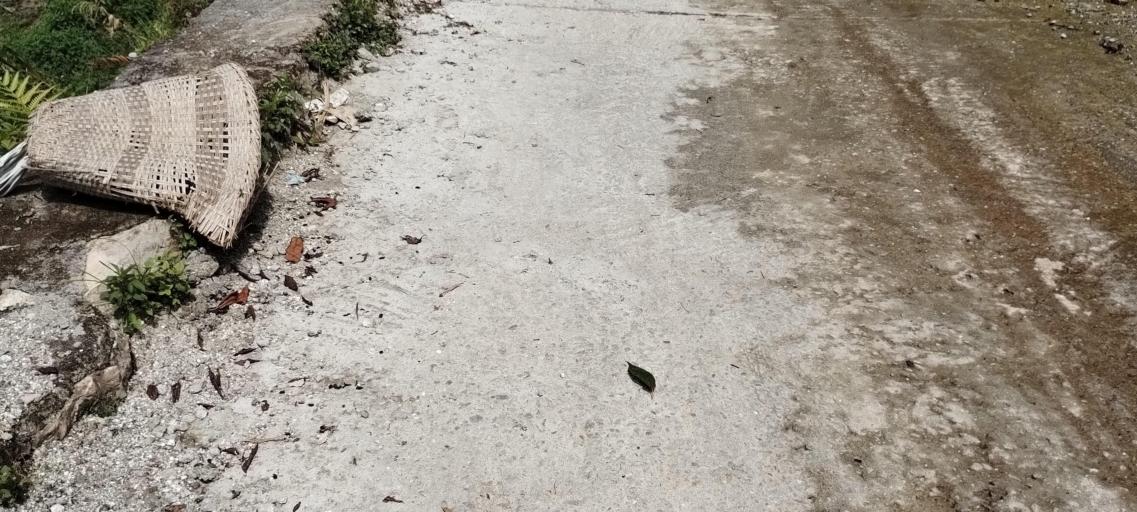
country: NP
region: Central Region
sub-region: Bagmati Zone
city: Kathmandu
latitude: 27.7915
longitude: 85.3592
